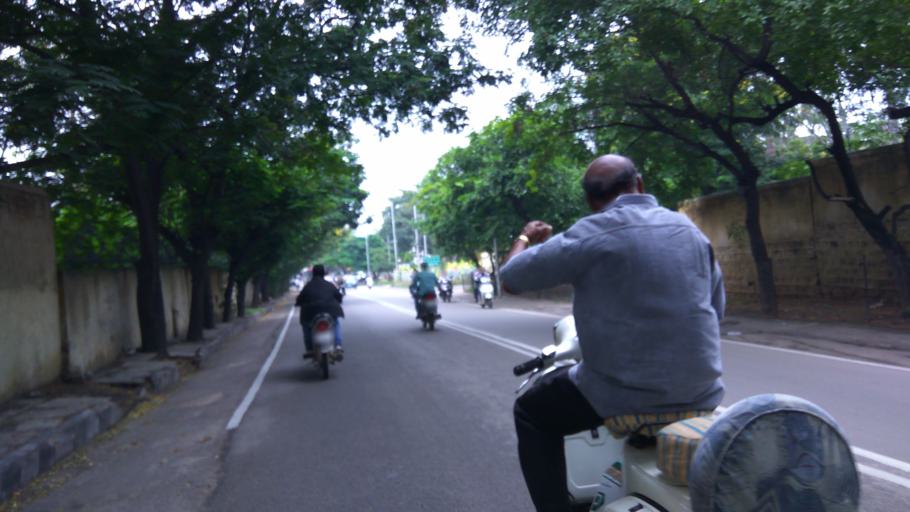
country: IN
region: Telangana
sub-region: Hyderabad
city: Malkajgiri
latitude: 17.4361
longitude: 78.5212
